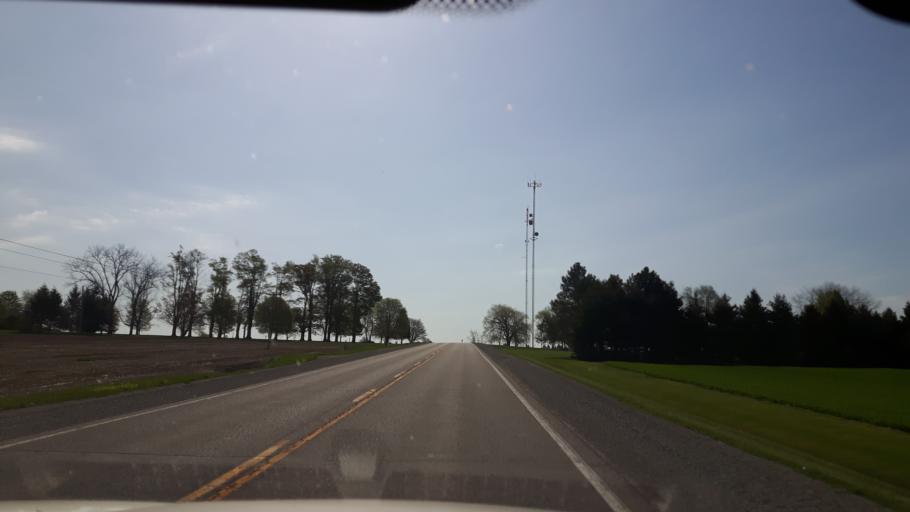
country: CA
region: Ontario
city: Bluewater
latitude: 43.5230
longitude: -81.5539
